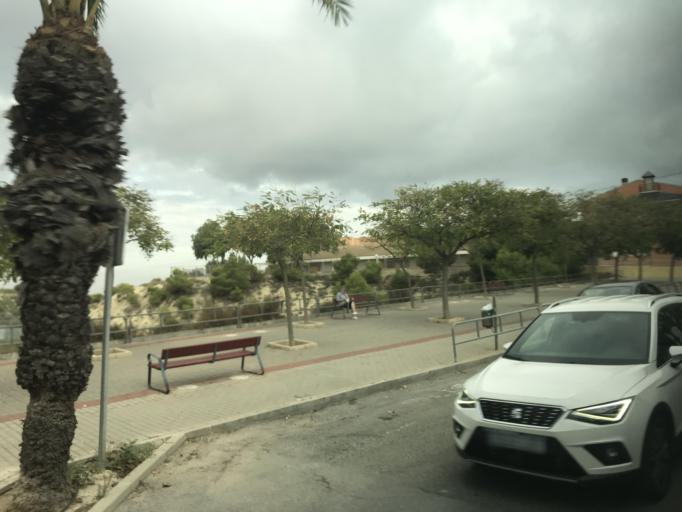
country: ES
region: Valencia
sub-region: Provincia de Alicante
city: Guardamar del Segura
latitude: 38.0855
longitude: -0.6554
